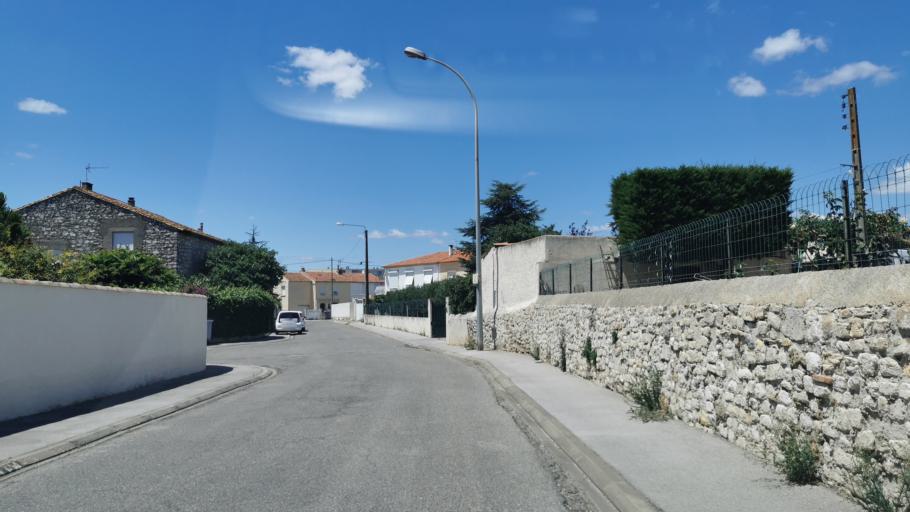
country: FR
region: Languedoc-Roussillon
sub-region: Departement de l'Aude
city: Narbonne
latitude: 43.1877
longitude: 3.0211
